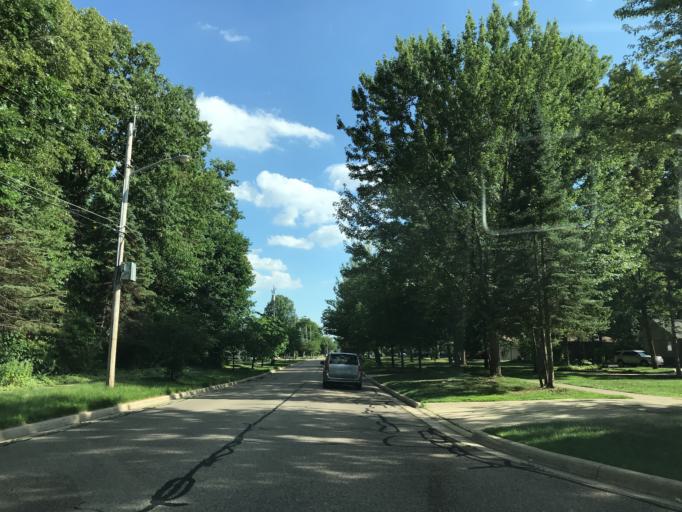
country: US
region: Michigan
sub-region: Oakland County
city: Farmington
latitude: 42.4208
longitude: -83.3942
